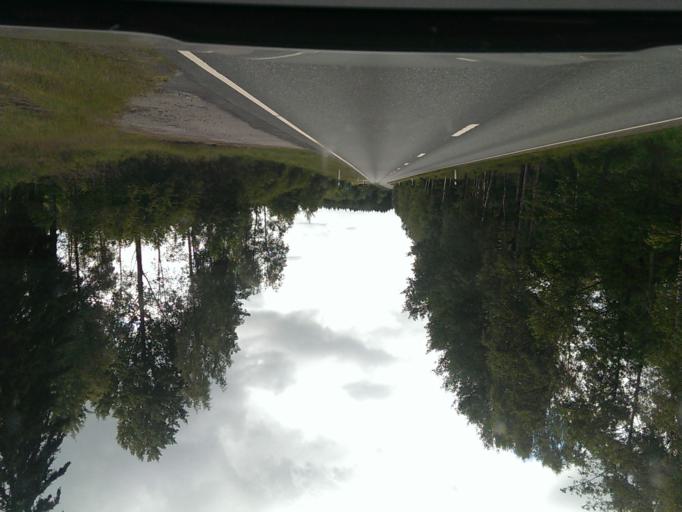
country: SE
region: Joenkoeping
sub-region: Varnamo Kommun
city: Varnamo
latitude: 57.2216
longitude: 14.0118
